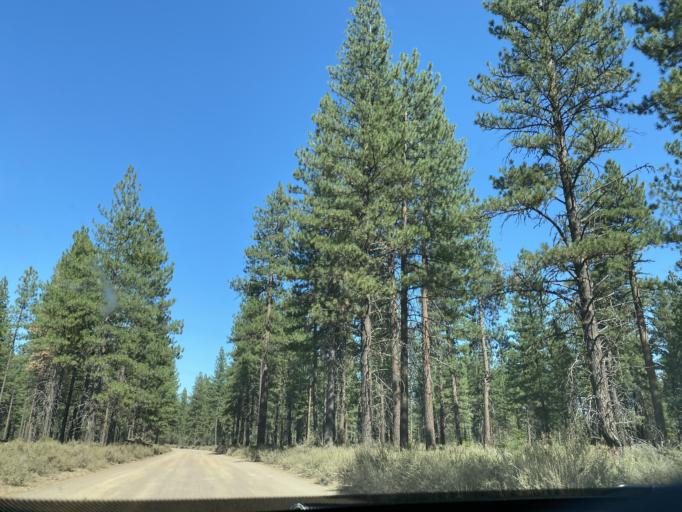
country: US
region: Oregon
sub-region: Deschutes County
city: Sunriver
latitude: 43.8747
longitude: -121.4710
